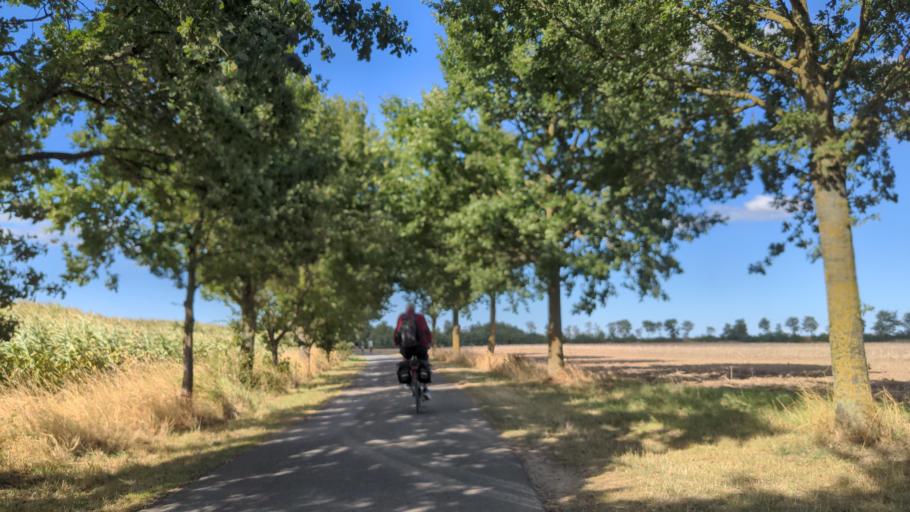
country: DE
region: Mecklenburg-Vorpommern
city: Wismar
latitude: 53.9242
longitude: 11.3945
